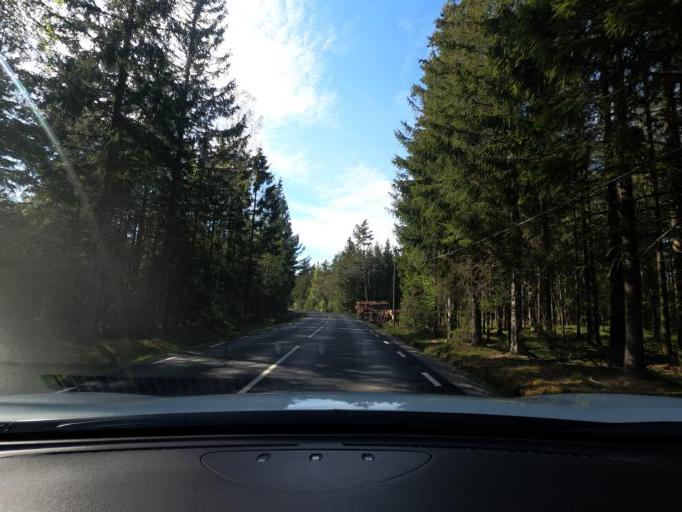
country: SE
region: Vaestra Goetaland
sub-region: Harryda Kommun
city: Landvetter
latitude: 57.6301
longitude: 12.2724
